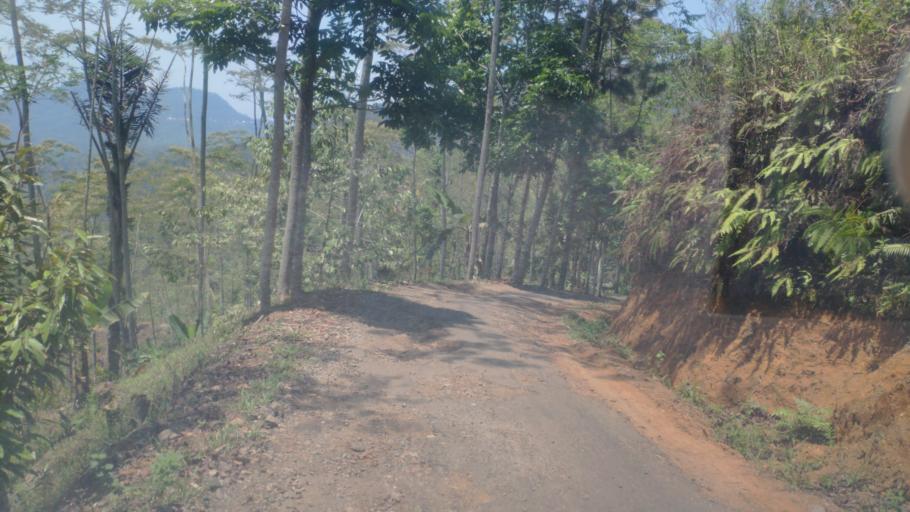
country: ID
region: Central Java
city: Buaran
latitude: -7.2866
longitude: 109.5898
